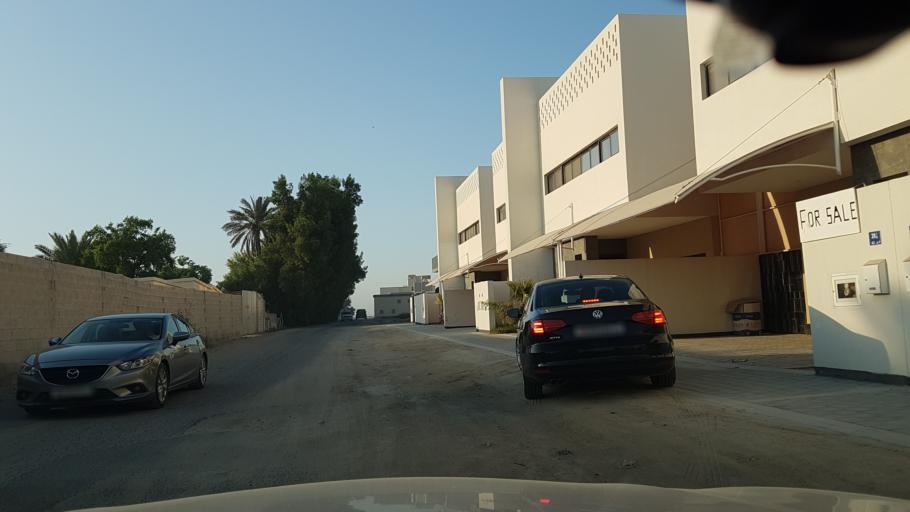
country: BH
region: Manama
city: Jidd Hafs
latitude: 26.2331
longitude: 50.5058
